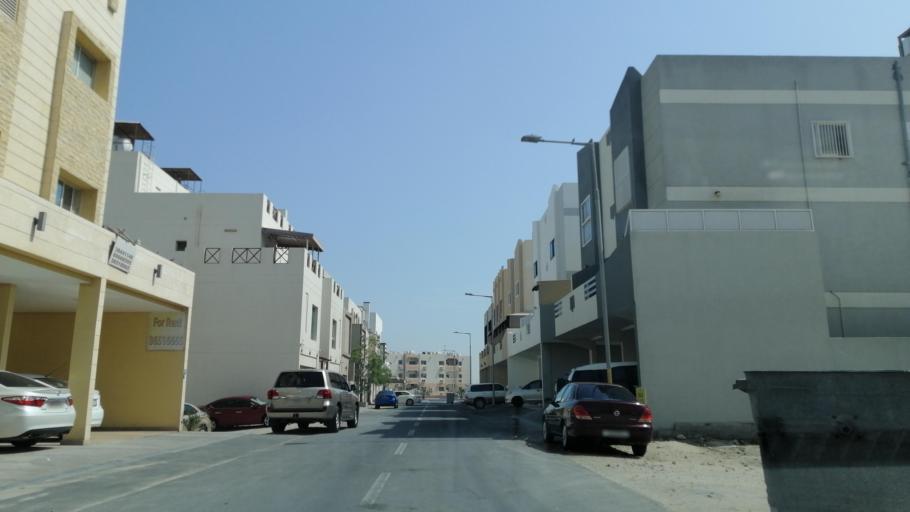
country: BH
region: Muharraq
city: Al Hadd
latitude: 26.2532
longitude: 50.6527
